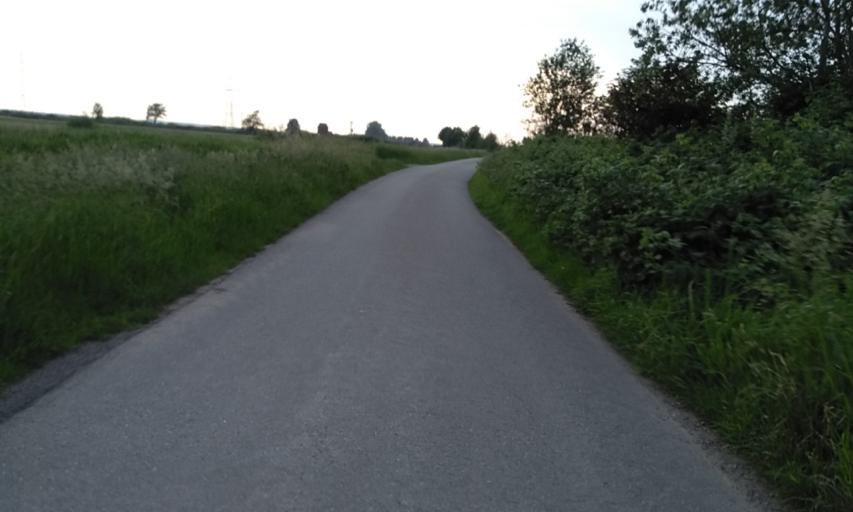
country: DE
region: Lower Saxony
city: Jork
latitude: 53.5022
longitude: 9.6524
